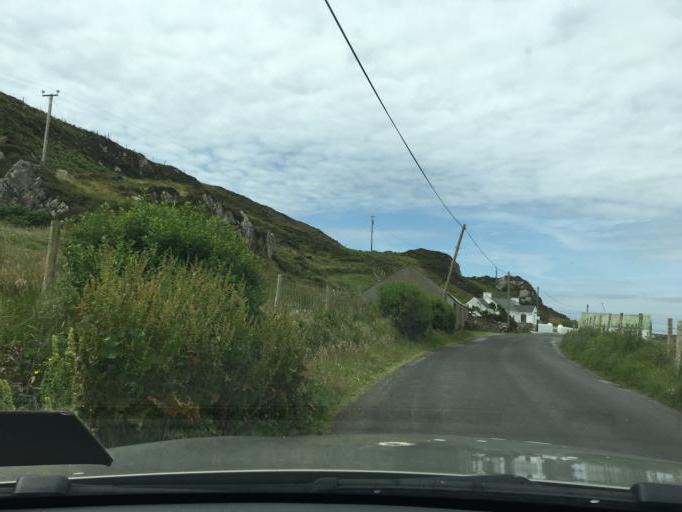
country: IE
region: Ulster
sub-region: County Donegal
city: Carndonagh
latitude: 55.3753
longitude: -7.3519
